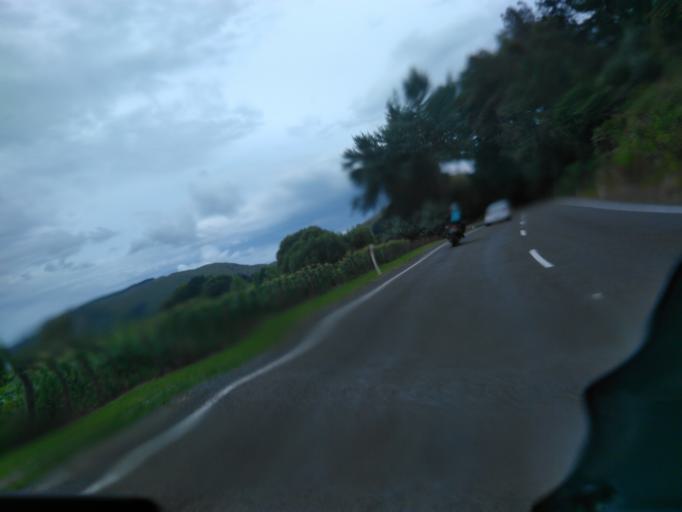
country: NZ
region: Gisborne
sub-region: Gisborne District
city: Gisborne
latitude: -38.4689
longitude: 177.8240
